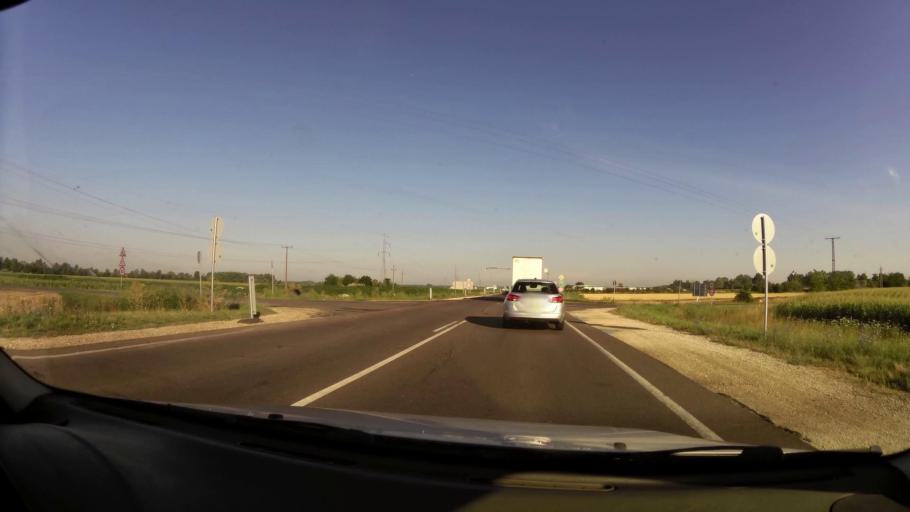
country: HU
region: Pest
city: Cegled
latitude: 47.2018
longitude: 19.7849
